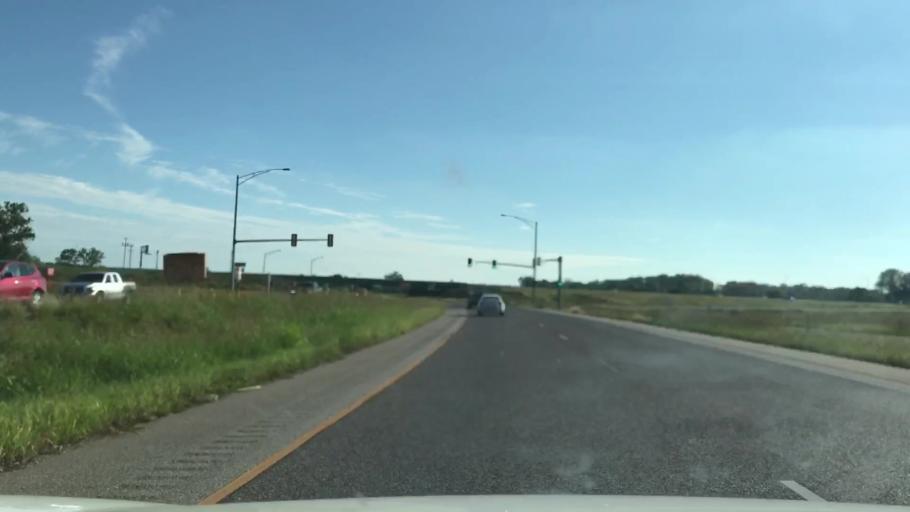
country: US
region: Illinois
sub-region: Madison County
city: Mitchell
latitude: 38.7690
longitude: -90.1230
